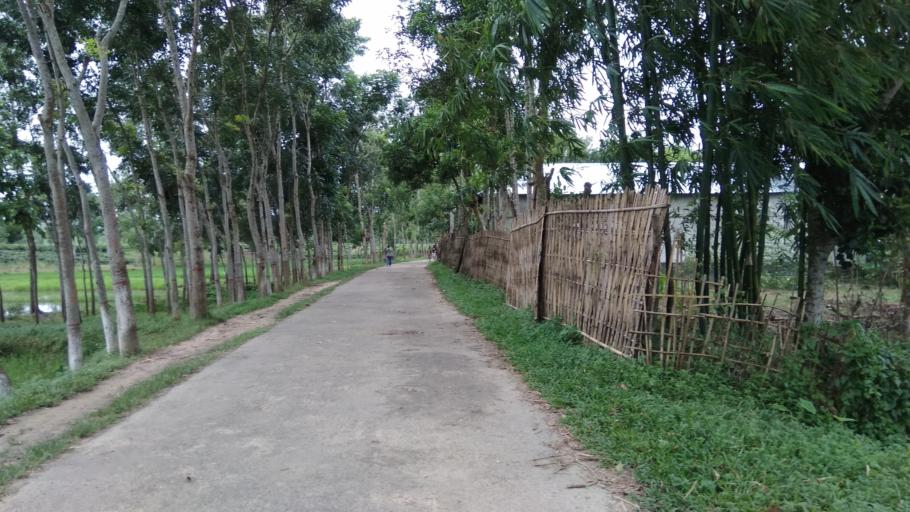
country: IN
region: Tripura
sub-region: Dhalai
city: Kamalpur
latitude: 24.2818
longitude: 91.8293
